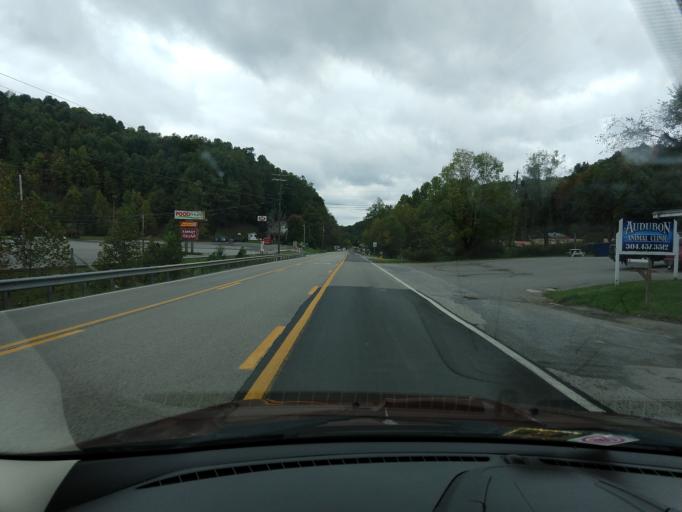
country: US
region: West Virginia
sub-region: Barbour County
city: Philippi
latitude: 39.1327
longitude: -80.0143
